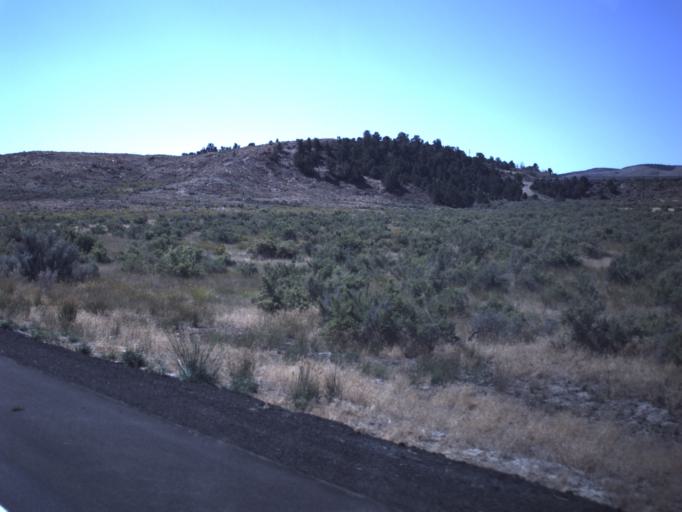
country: US
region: Utah
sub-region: Utah County
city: Eagle Mountain
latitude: 39.9987
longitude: -112.2732
